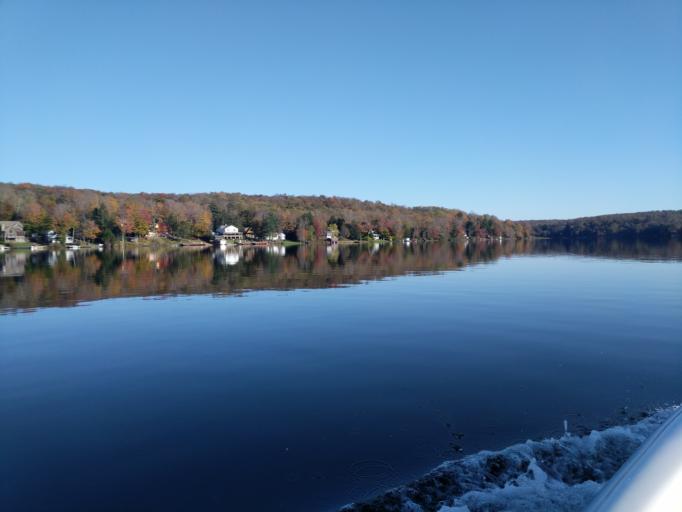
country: US
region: New York
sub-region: Sullivan County
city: Livingston Manor
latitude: 41.8899
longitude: -74.9799
